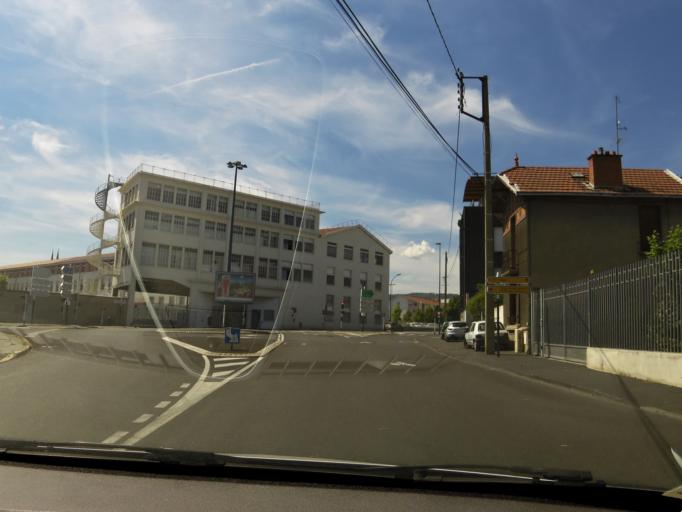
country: FR
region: Auvergne
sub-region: Departement du Puy-de-Dome
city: Clermont-Ferrand
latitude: 45.7869
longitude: 3.0918
